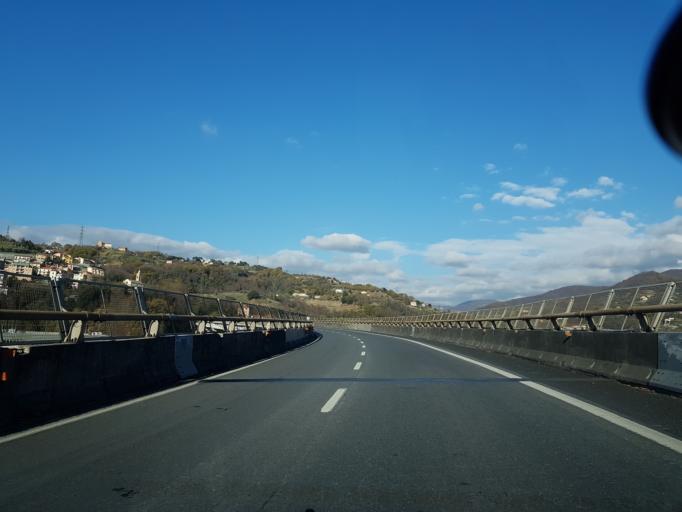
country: IT
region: Liguria
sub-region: Provincia di Genova
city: Manesseno
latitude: 44.4712
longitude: 8.9108
